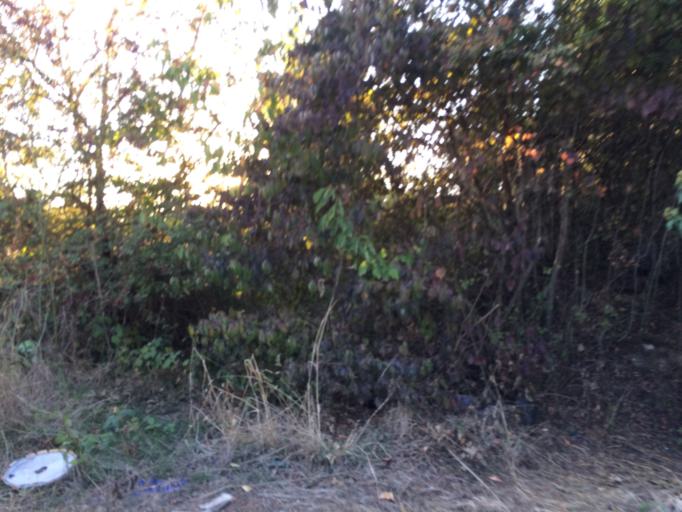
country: FR
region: Ile-de-France
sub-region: Departement de l'Essonne
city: Champlan
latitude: 48.7162
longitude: 2.2741
